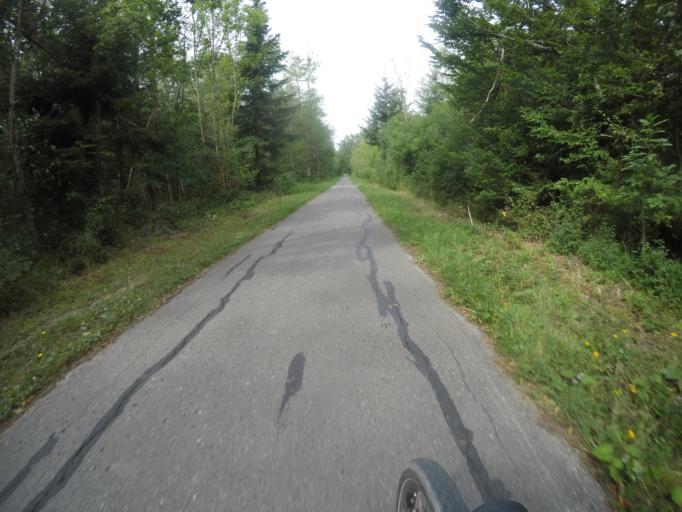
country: DE
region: Baden-Wuerttemberg
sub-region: Karlsruhe Region
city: Eutingen
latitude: 48.8700
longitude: 8.7674
